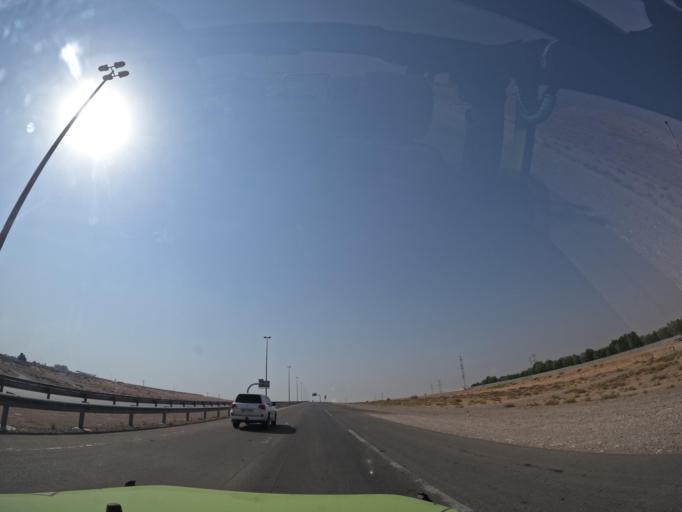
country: OM
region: Al Buraimi
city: Al Buraymi
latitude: 24.3812
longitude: 55.7272
